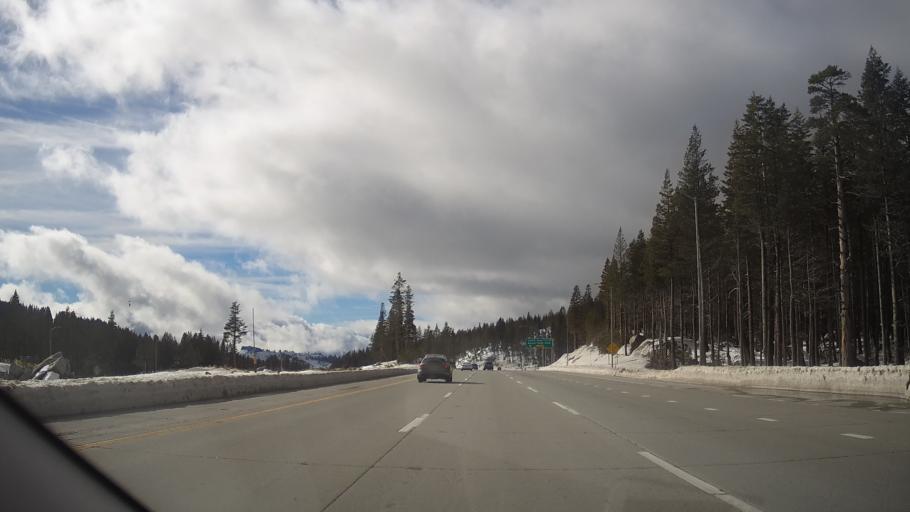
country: US
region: California
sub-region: Nevada County
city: Truckee
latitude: 39.3409
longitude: -120.3445
